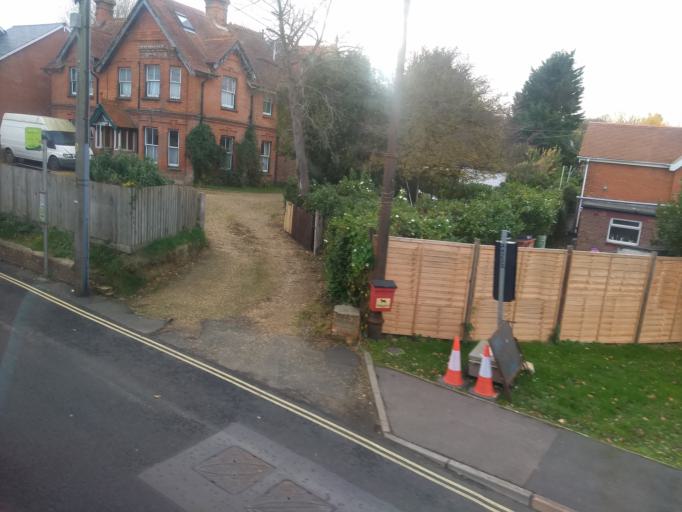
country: GB
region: England
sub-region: Isle of Wight
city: Newport
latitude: 50.6955
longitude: -1.3207
